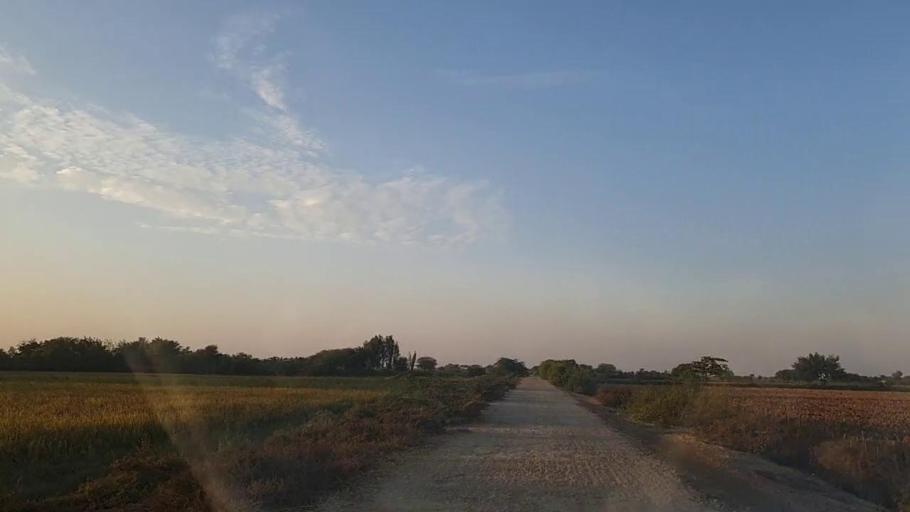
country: PK
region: Sindh
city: Chuhar Jamali
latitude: 24.4519
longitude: 68.1180
